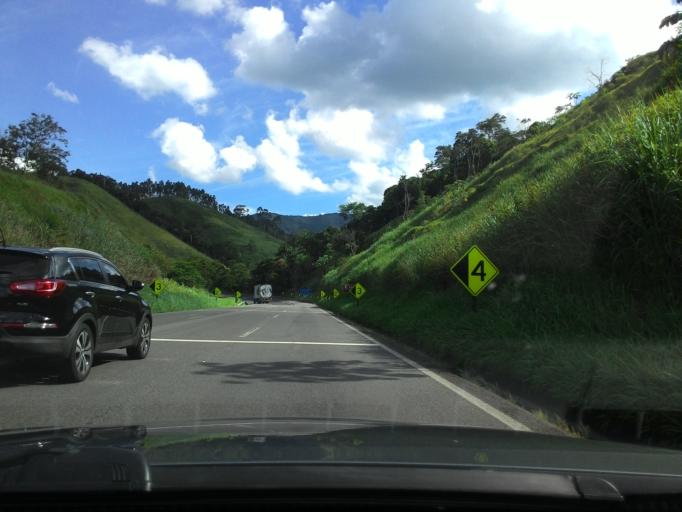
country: BR
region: Sao Paulo
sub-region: Cajati
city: Cajati
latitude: -24.8346
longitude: -48.2226
